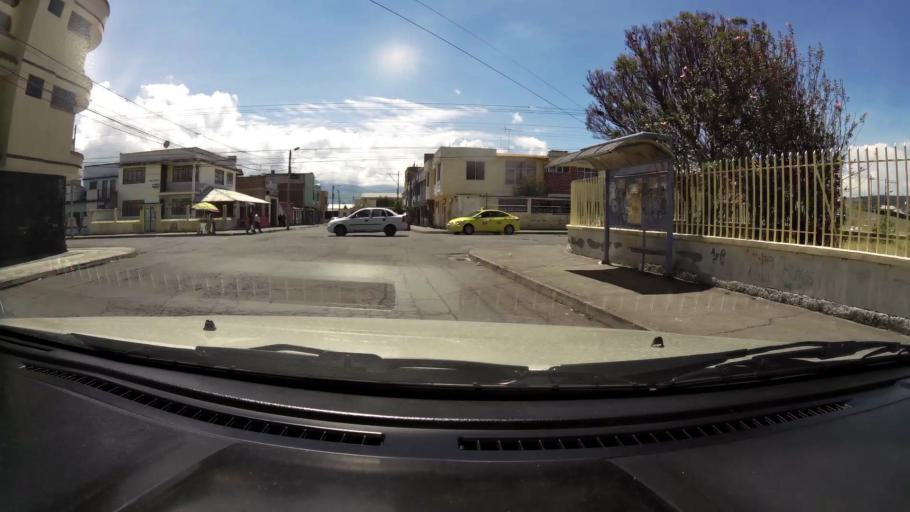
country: EC
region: Chimborazo
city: Riobamba
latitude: -1.6788
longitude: -78.6521
